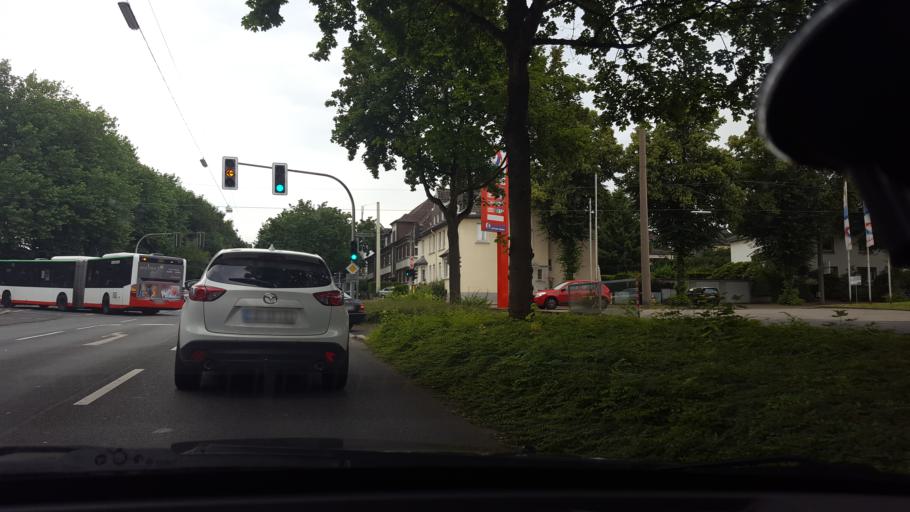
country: DE
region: North Rhine-Westphalia
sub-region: Regierungsbezirk Munster
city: Recklinghausen
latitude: 51.6242
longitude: 7.1930
